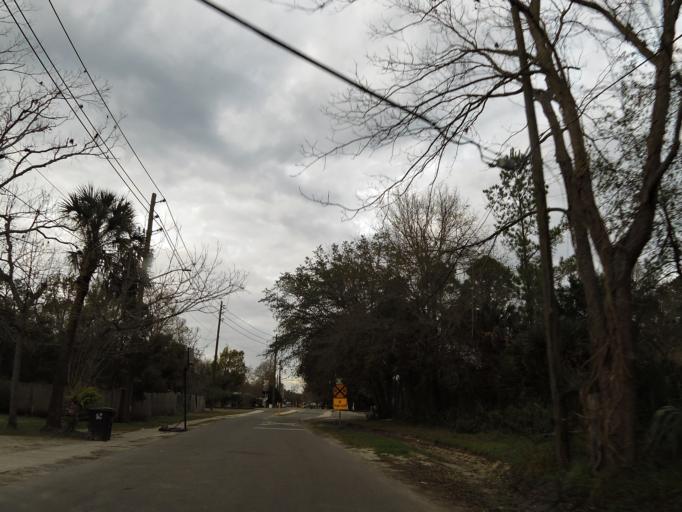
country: US
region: Florida
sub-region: Duval County
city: Baldwin
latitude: 30.2993
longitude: -81.9788
